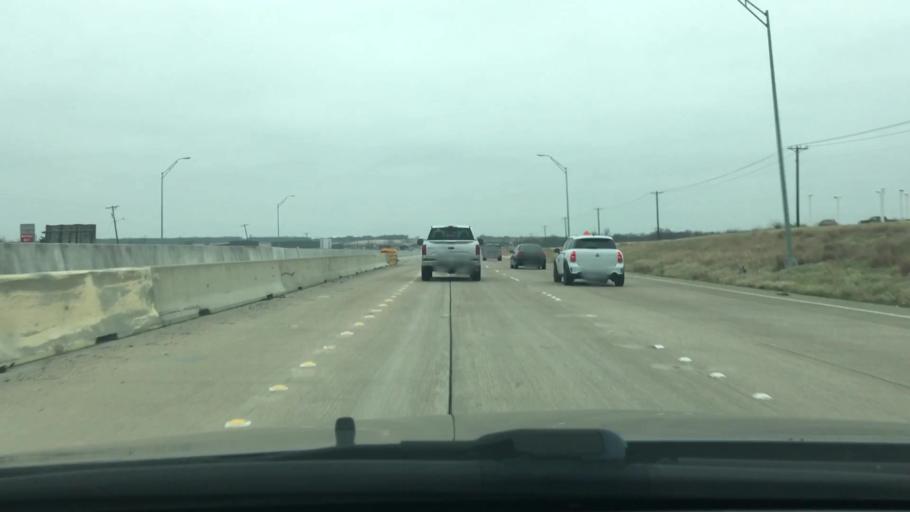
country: US
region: Texas
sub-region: Navarro County
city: Corsicana
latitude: 32.0569
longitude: -96.4512
